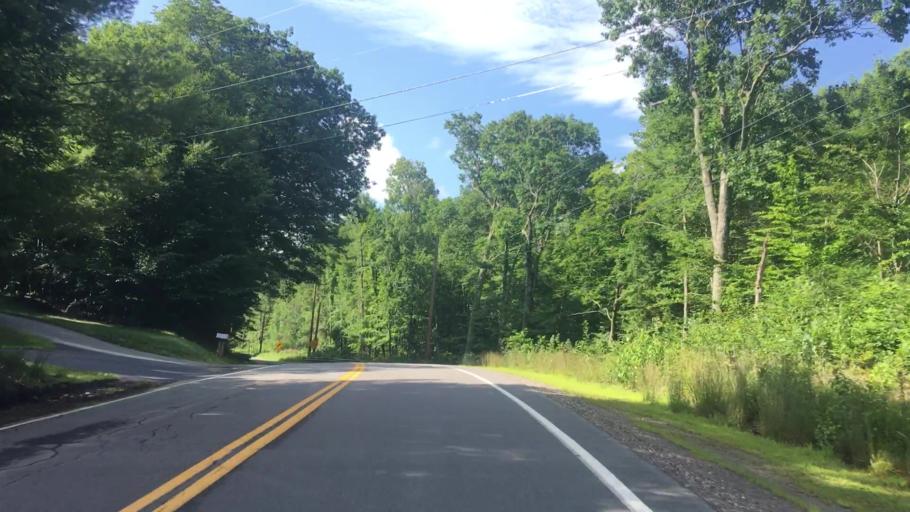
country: US
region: New Hampshire
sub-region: Belknap County
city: Gilford
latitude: 43.5367
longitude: -71.3220
